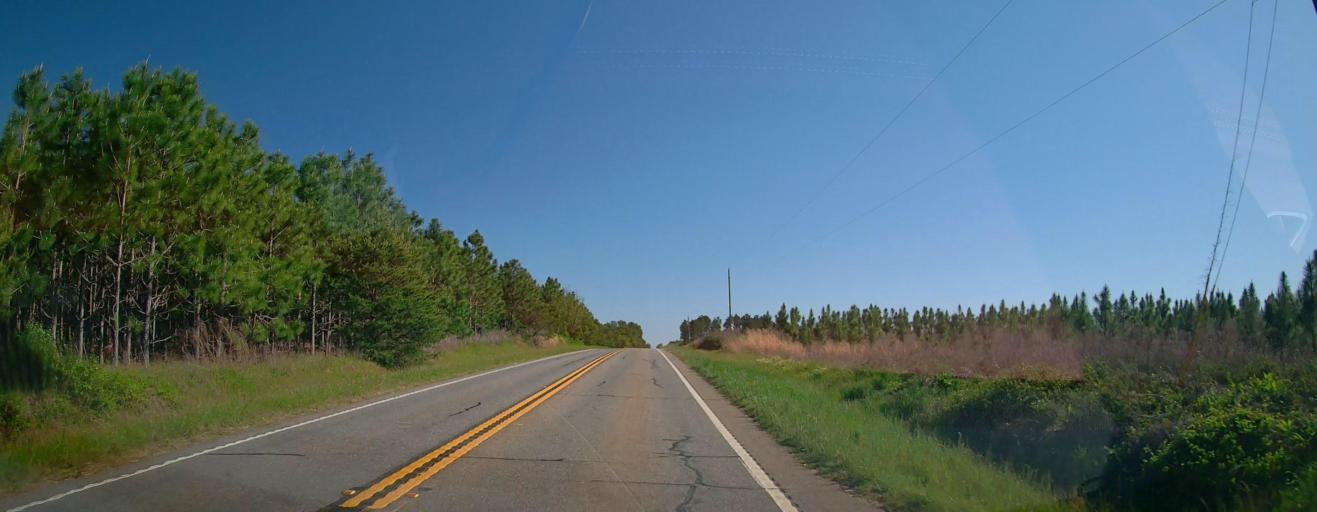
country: US
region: Georgia
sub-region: Wilcox County
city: Rochelle
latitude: 31.8361
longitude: -83.4890
